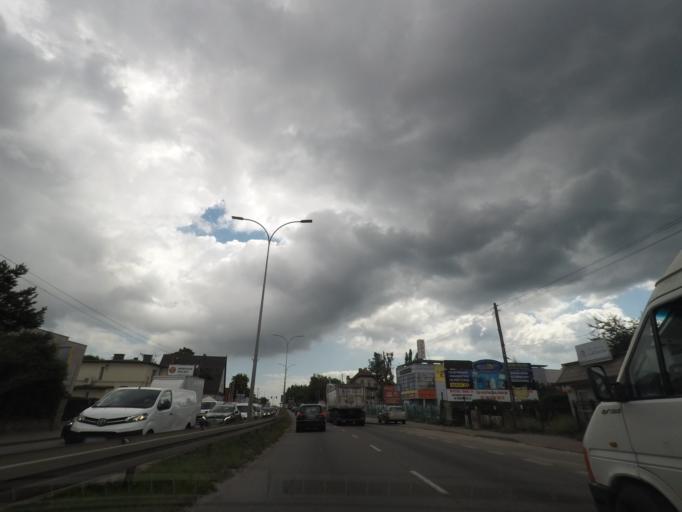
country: PL
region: Pomeranian Voivodeship
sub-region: Powiat wejherowski
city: Rumia
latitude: 54.5634
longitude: 18.3931
